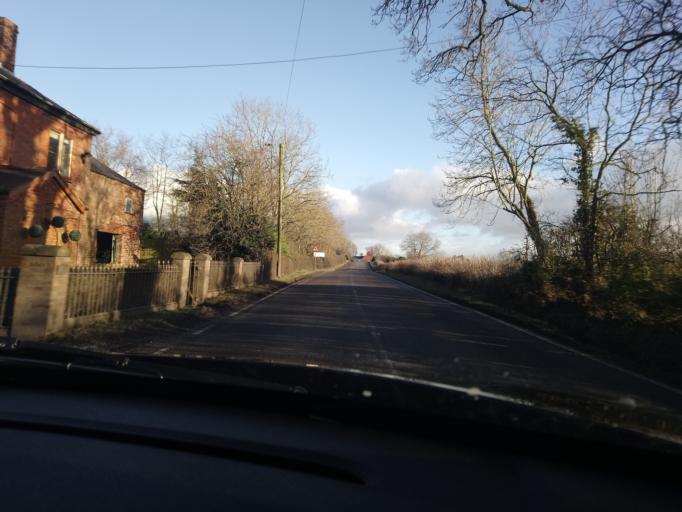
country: GB
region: England
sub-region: Shropshire
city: Ellesmere
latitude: 52.9183
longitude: -2.9207
